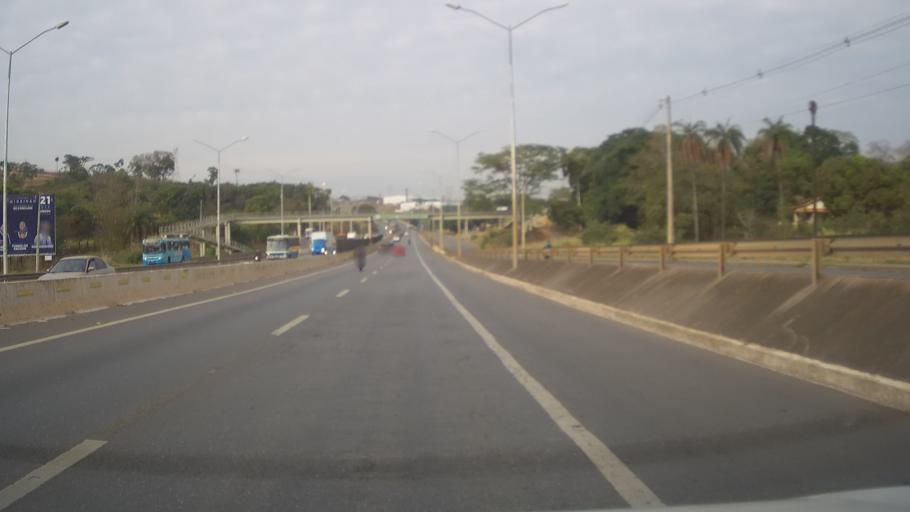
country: BR
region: Minas Gerais
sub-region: Vespasiano
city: Vespasiano
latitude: -19.7264
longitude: -43.9375
